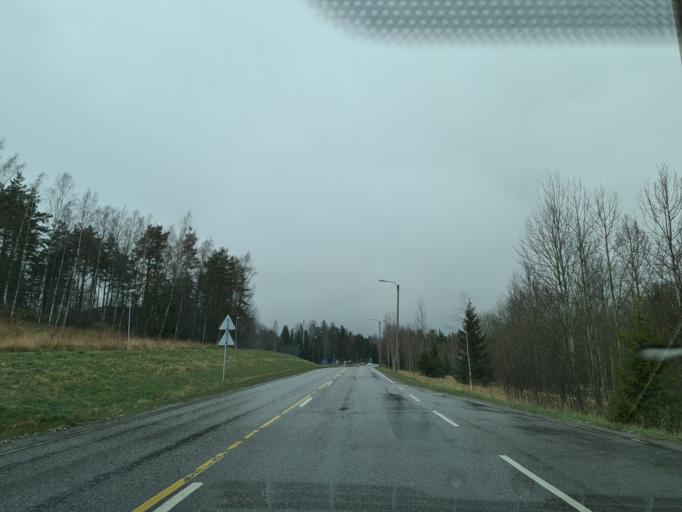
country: FI
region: Uusimaa
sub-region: Helsinki
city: Kirkkonummi
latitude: 60.0920
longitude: 24.4107
